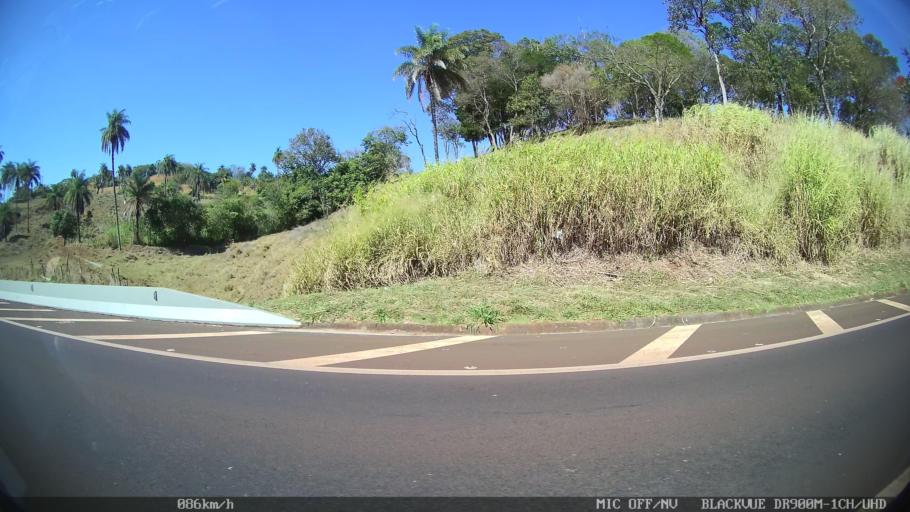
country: BR
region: Sao Paulo
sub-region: Franca
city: Franca
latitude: -20.6047
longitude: -47.4492
